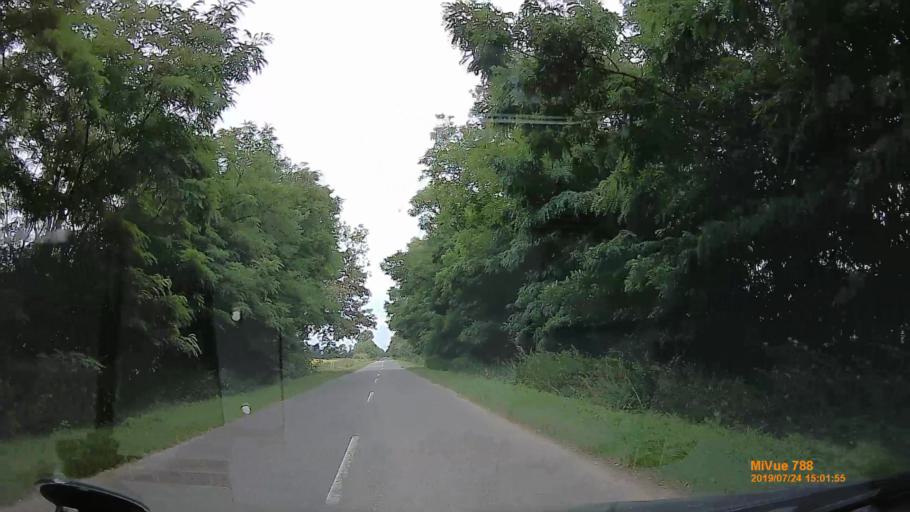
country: HU
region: Szabolcs-Szatmar-Bereg
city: Vasarosnameny
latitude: 48.2267
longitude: 22.3977
